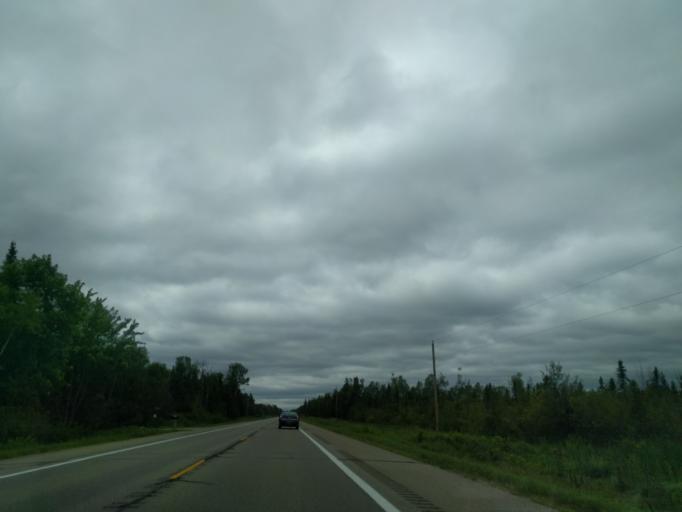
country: US
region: Michigan
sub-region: Delta County
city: Escanaba
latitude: 45.6191
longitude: -87.2127
